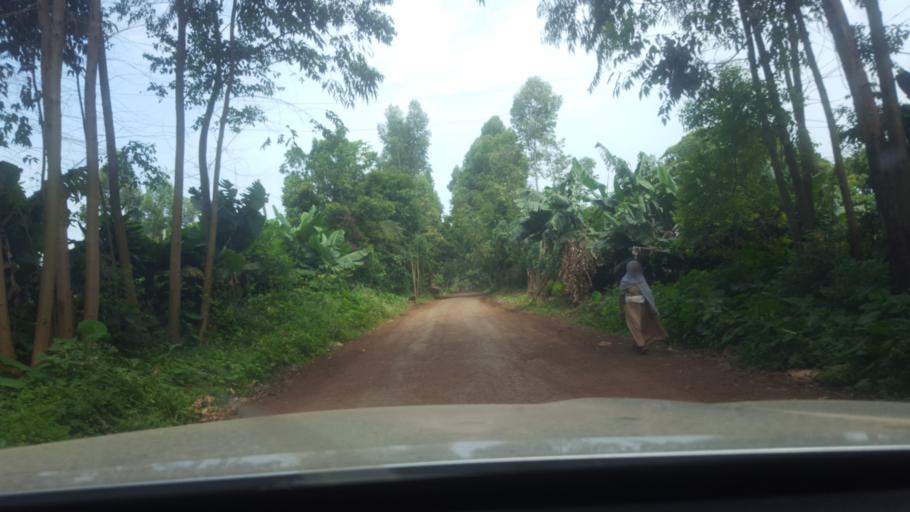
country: ET
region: Southern Nations, Nationalities, and People's Region
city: Tippi
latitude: 7.2497
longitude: 35.3675
